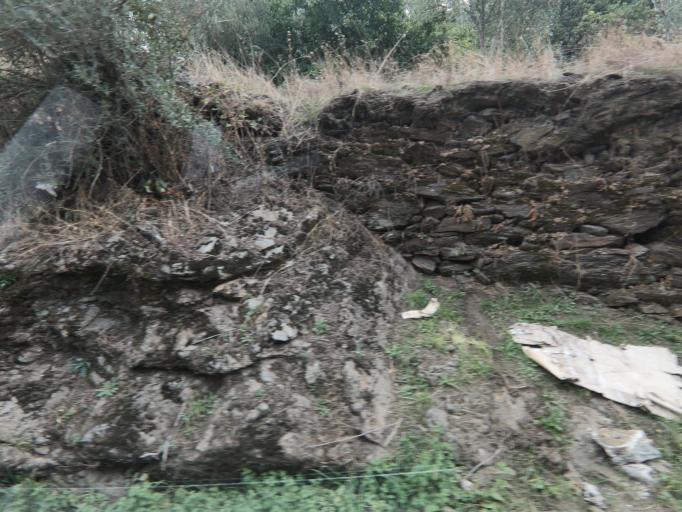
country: PT
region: Vila Real
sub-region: Mondim de Basto
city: Mondim de Basto
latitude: 41.3568
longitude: -7.8891
